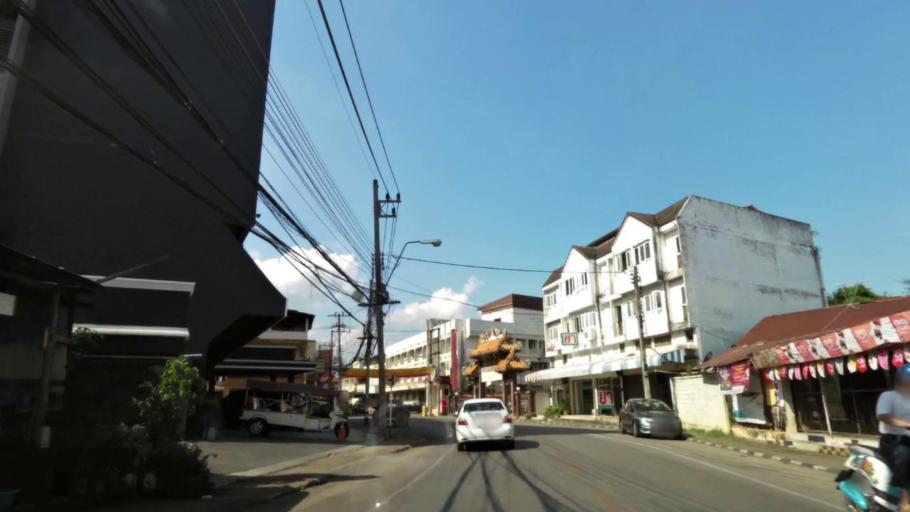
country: TH
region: Phrae
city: Phrae
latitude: 18.1403
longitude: 100.1429
